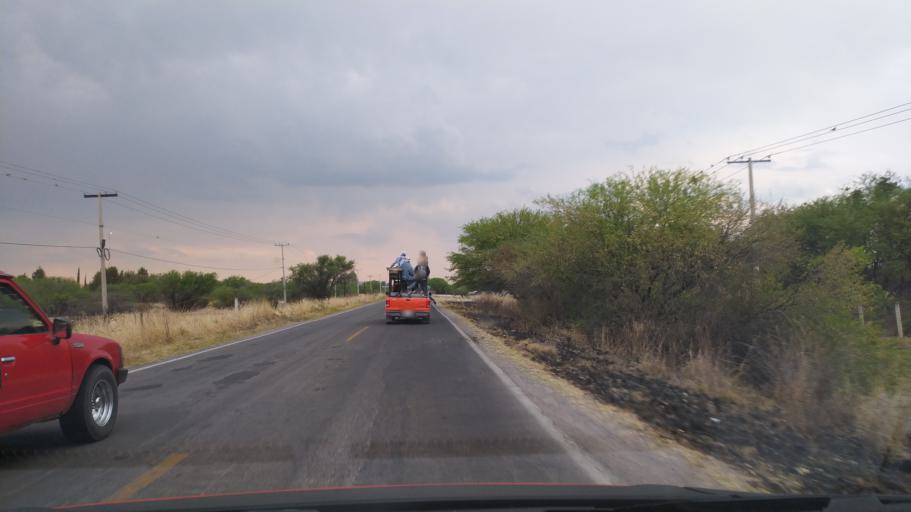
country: MX
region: Guanajuato
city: Ciudad Manuel Doblado
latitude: 20.8070
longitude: -101.9049
